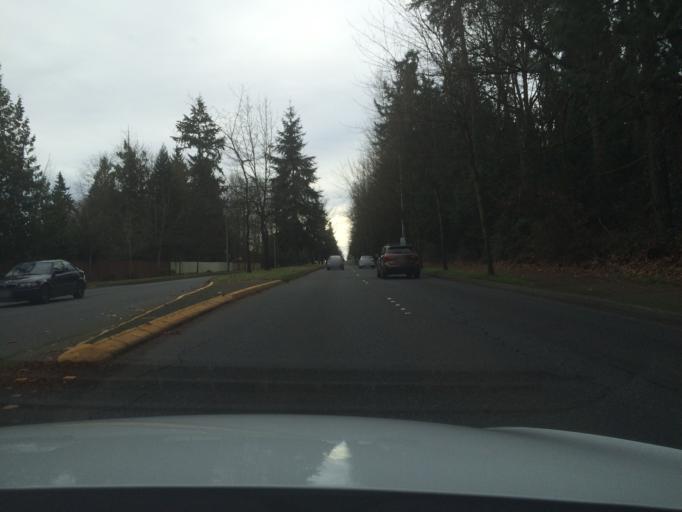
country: US
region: Washington
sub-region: King County
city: Redmond
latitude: 47.6744
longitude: -122.1431
